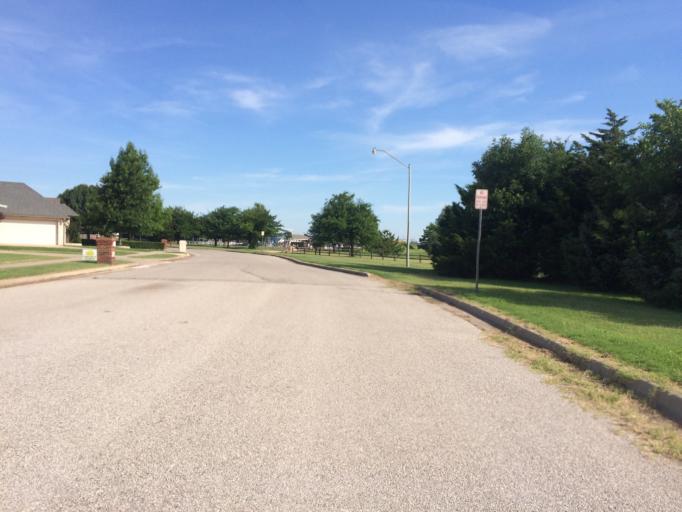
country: US
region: Oklahoma
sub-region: Cleveland County
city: Norman
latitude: 35.2288
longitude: -97.4768
